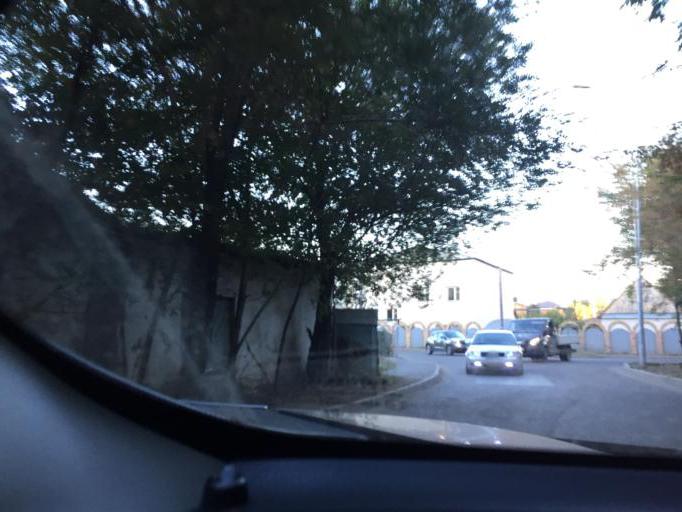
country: KZ
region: Astana Qalasy
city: Astana
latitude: 51.1474
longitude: 71.4269
